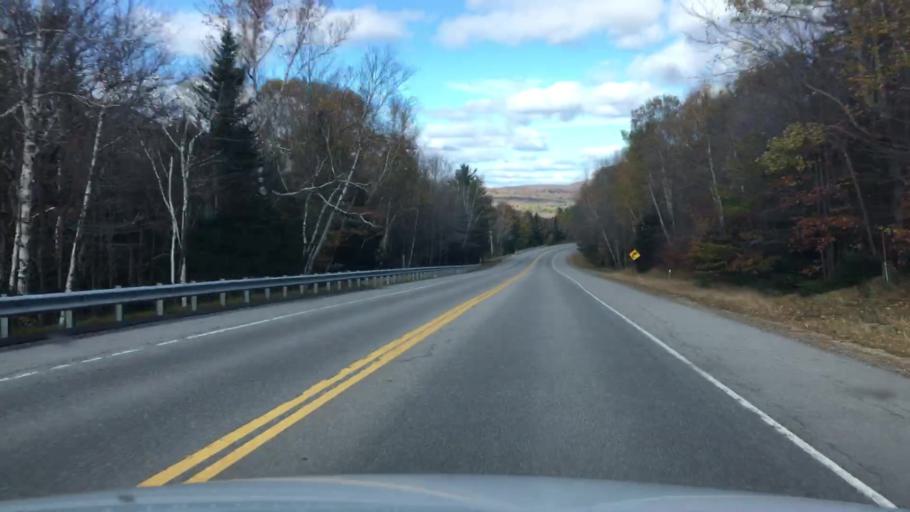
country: US
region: New Hampshire
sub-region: Coos County
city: Gorham
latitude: 44.3188
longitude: -71.2171
